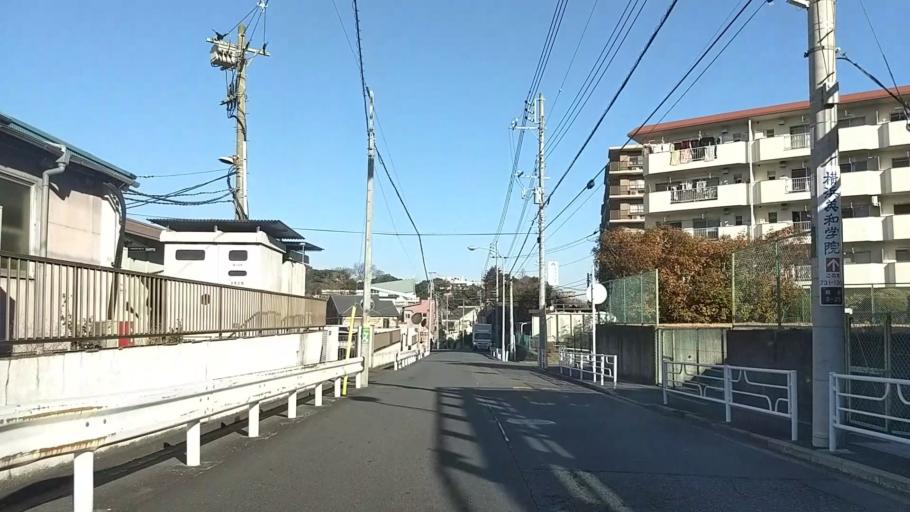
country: JP
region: Kanagawa
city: Yokohama
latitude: 35.4227
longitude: 139.6119
